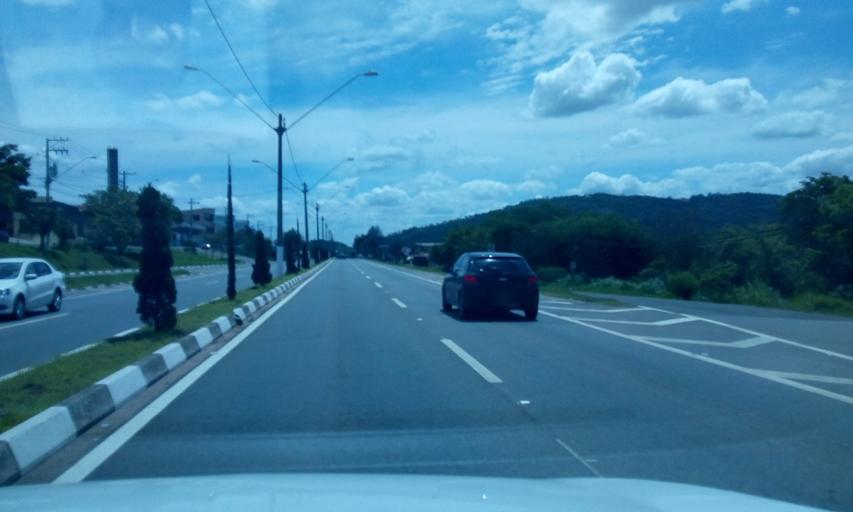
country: BR
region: Sao Paulo
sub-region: Itupeva
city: Itupeva
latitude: -23.1564
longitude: -47.0429
